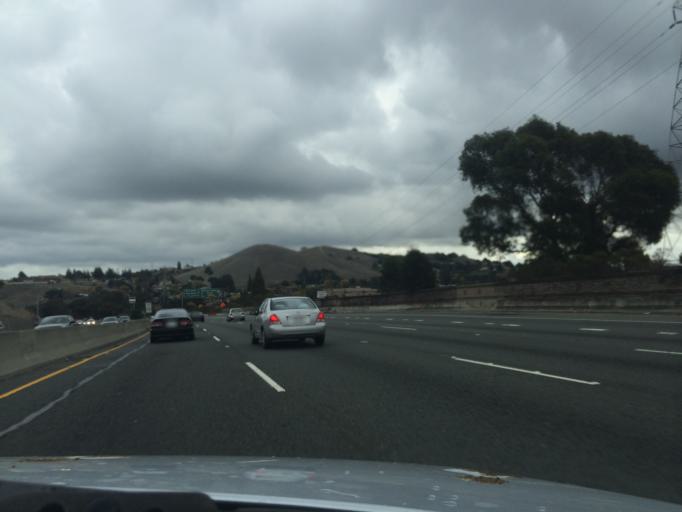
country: US
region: California
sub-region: Contra Costa County
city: Pinole
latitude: 37.9947
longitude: -122.2923
